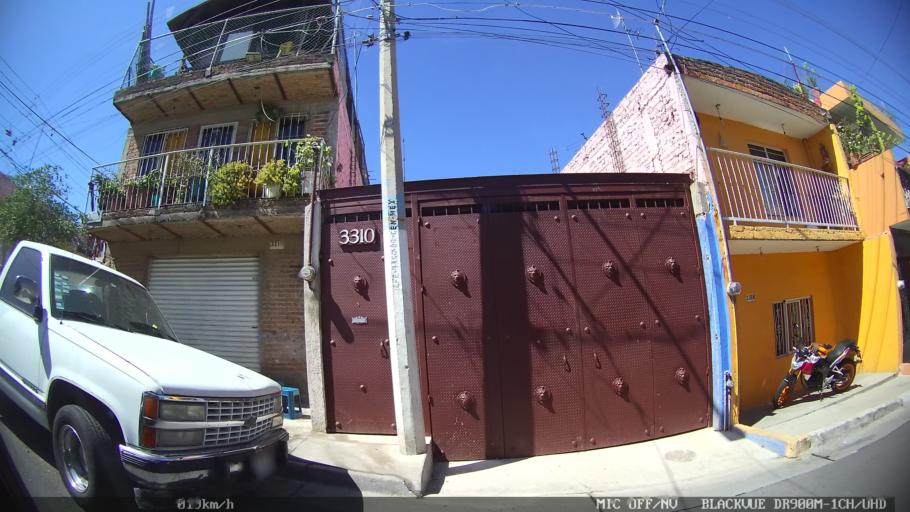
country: MX
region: Jalisco
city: Tlaquepaque
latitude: 20.6938
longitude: -103.2842
